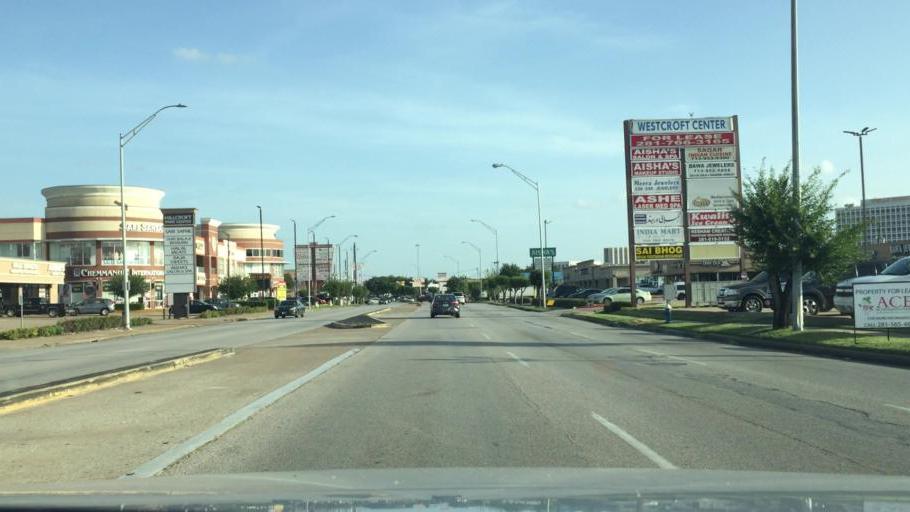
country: US
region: Texas
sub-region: Harris County
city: Piney Point Village
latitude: 29.7218
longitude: -95.5012
